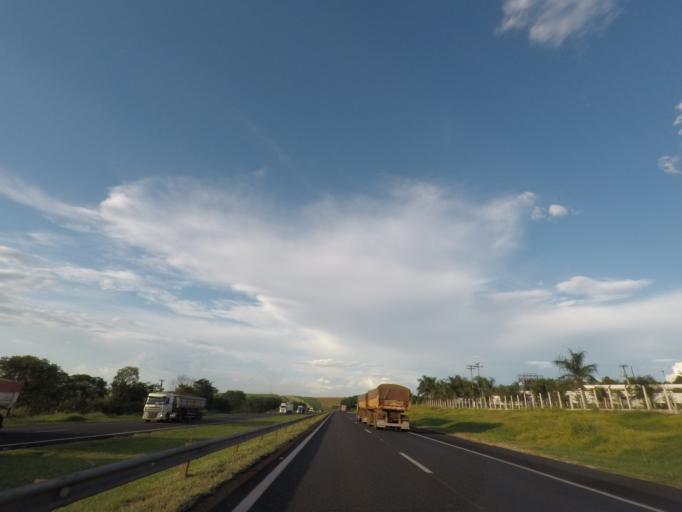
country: BR
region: Sao Paulo
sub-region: Ituverava
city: Ituverava
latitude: -20.2949
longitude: -47.7986
